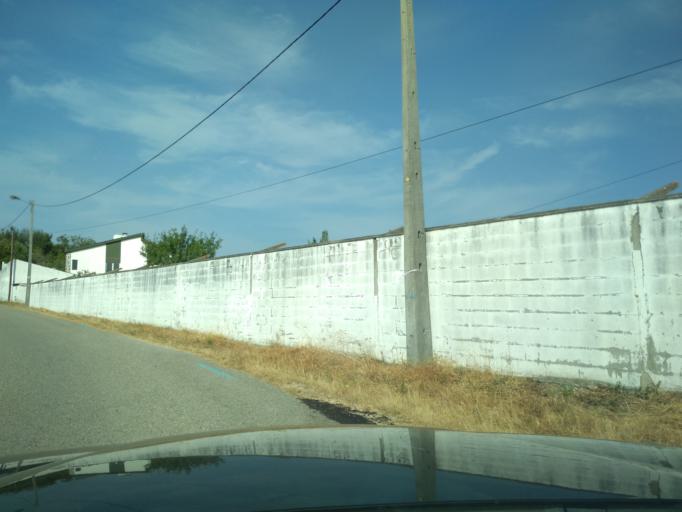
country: PT
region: Coimbra
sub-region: Condeixa-A-Nova
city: Condeixa-a-Nova
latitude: 40.1319
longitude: -8.4767
